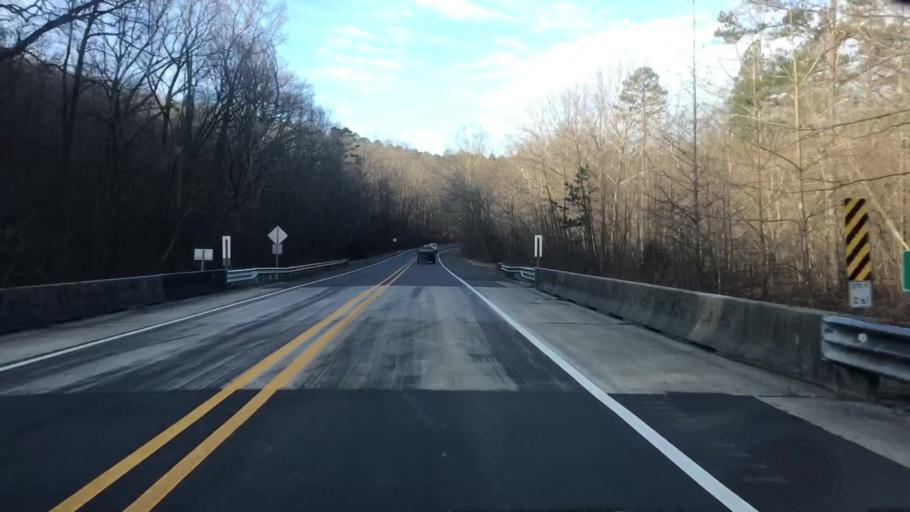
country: US
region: Arkansas
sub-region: Montgomery County
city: Mount Ida
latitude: 34.5231
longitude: -93.3955
